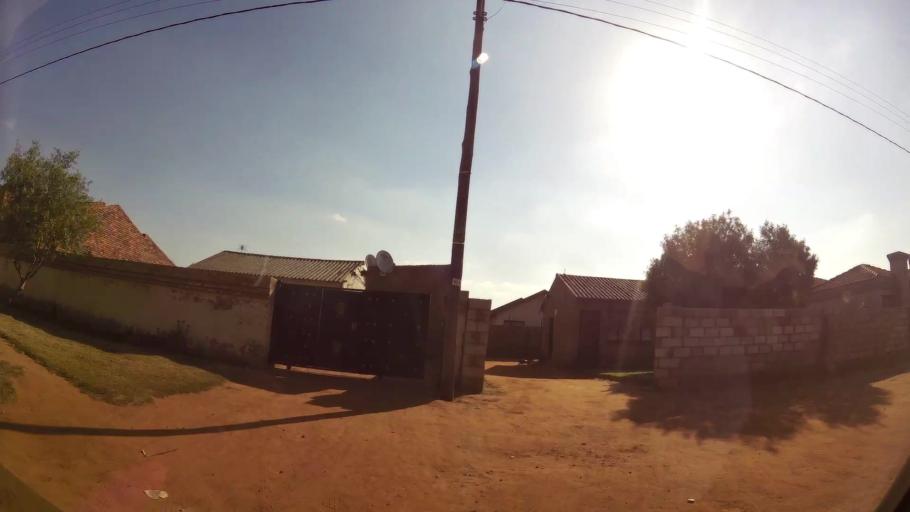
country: ZA
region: Gauteng
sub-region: Ekurhuleni Metropolitan Municipality
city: Benoni
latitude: -26.2256
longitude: 28.3279
